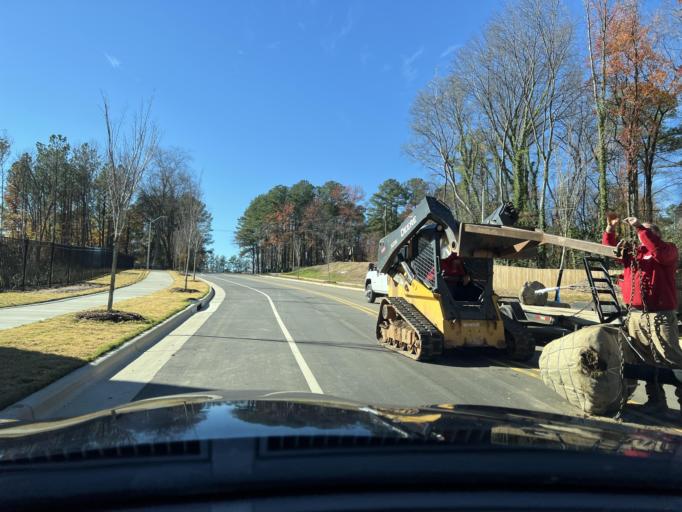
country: US
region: North Carolina
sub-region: Wake County
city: Raleigh
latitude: 35.8193
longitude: -78.5992
